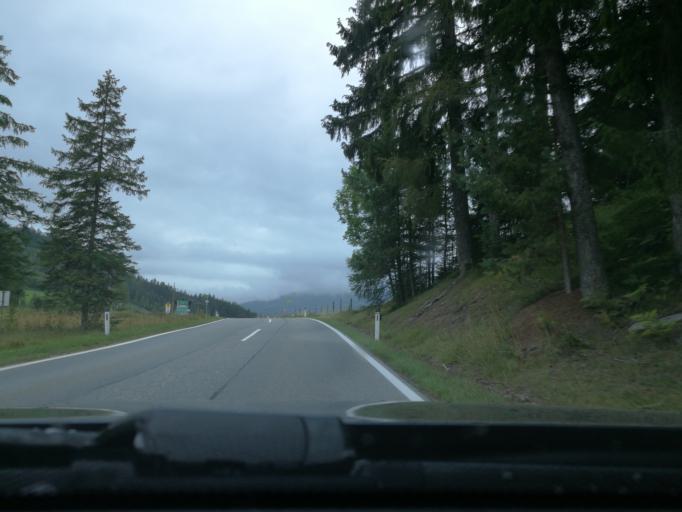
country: AT
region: Salzburg
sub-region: Politischer Bezirk Sankt Johann im Pongau
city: Forstau
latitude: 47.3784
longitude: 13.5153
